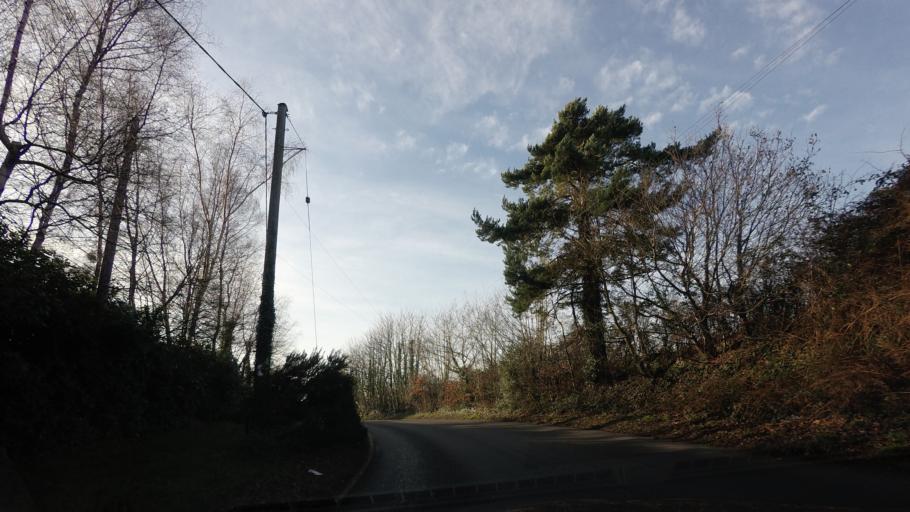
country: GB
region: England
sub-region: East Sussex
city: Bexhill-on-Sea
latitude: 50.8862
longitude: 0.4280
